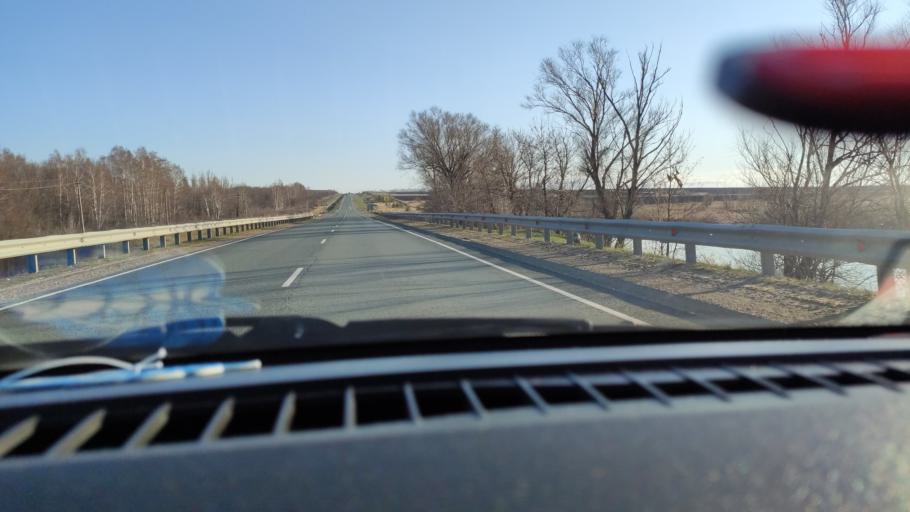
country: RU
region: Saratov
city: Alekseyevka
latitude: 52.2480
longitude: 47.9100
